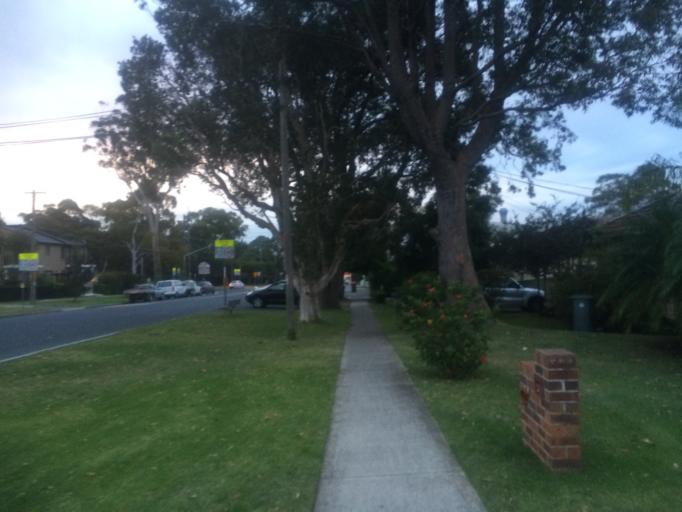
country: AU
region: New South Wales
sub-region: Sutherland Shire
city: Kirrawee
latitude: -34.0286
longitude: 151.0678
